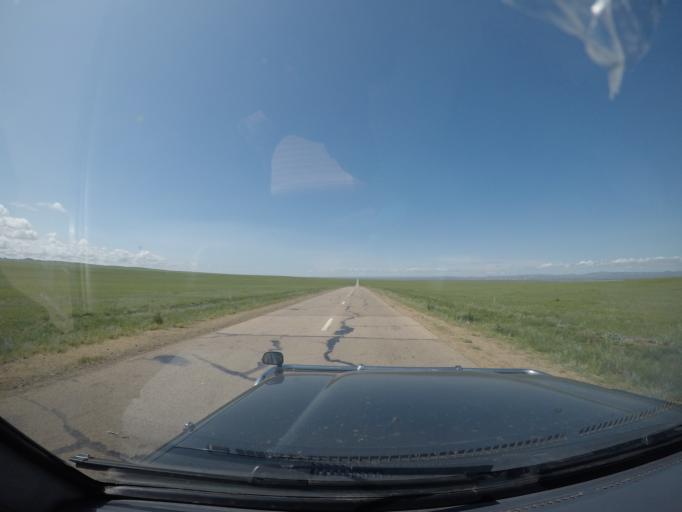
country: MN
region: Hentiy
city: Bayan
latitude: 47.2795
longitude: 110.8218
